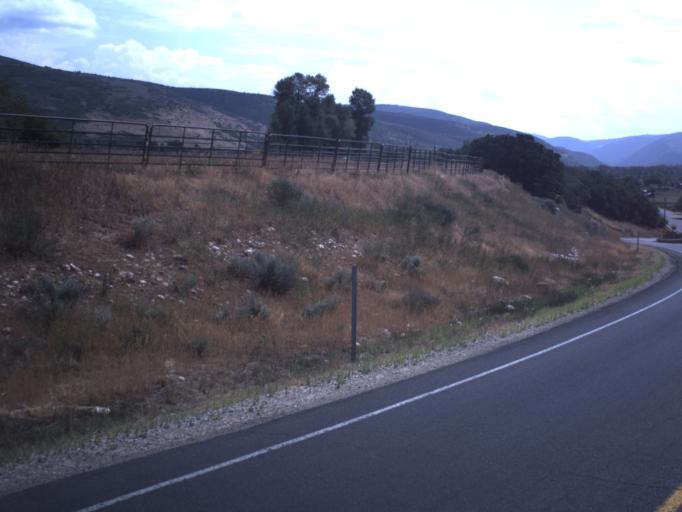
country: US
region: Utah
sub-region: Summit County
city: Francis
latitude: 40.5859
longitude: -111.2419
